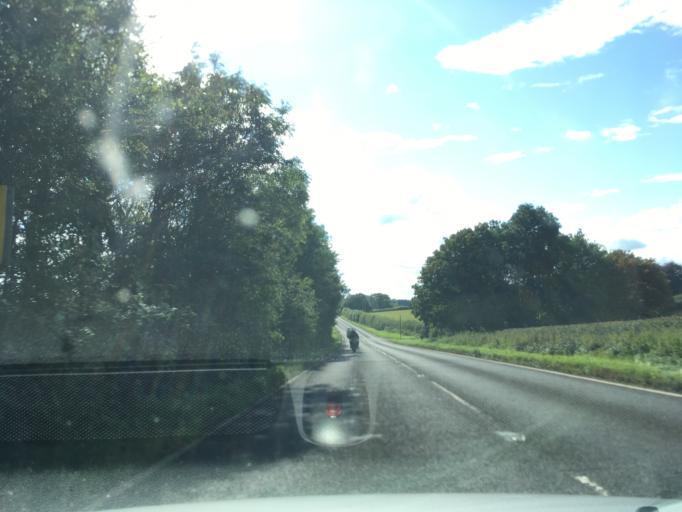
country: GB
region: England
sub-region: Oxfordshire
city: Claydon
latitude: 52.1309
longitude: -1.2804
